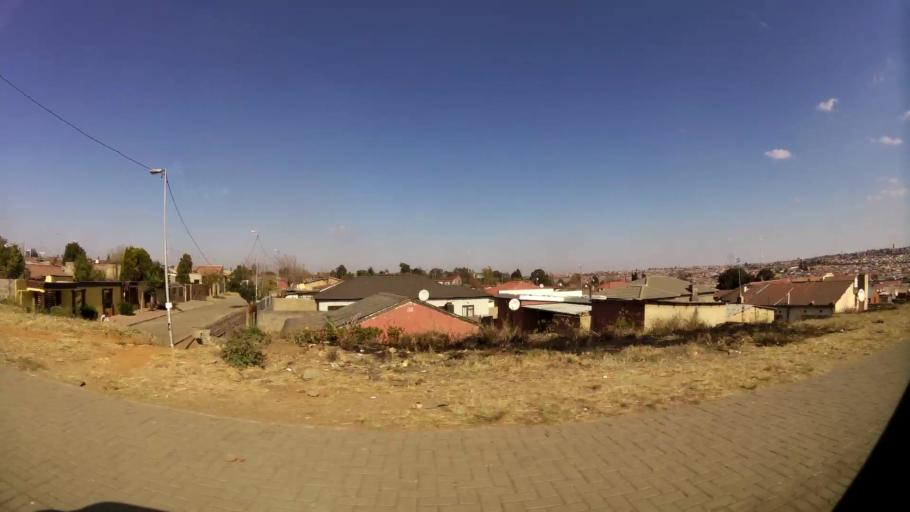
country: ZA
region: Gauteng
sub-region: City of Johannesburg Metropolitan Municipality
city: Soweto
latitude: -26.2262
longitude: 27.9308
